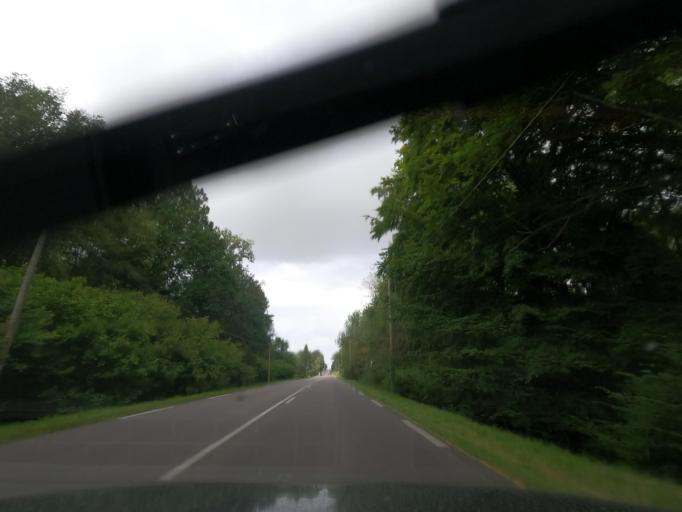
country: FR
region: Haute-Normandie
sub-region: Departement de l'Eure
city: Menneval
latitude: 49.1259
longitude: 0.6352
